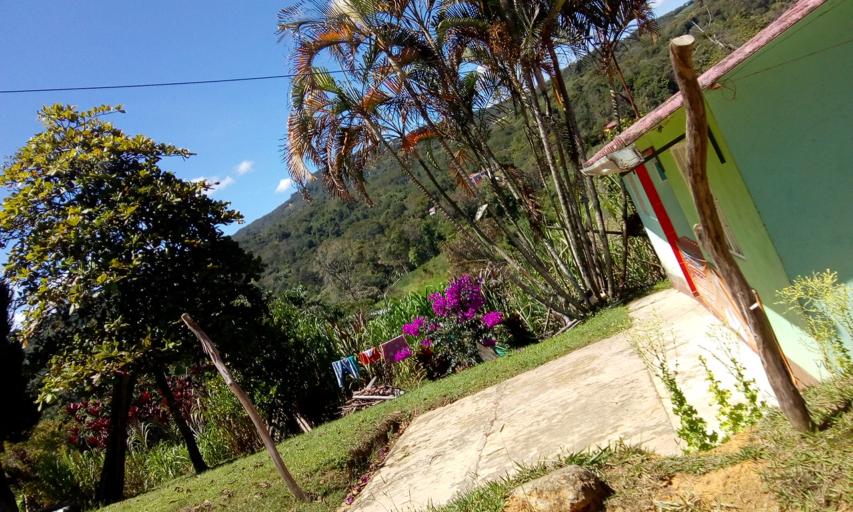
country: CO
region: Santander
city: Guepsa
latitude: 6.0076
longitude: -73.5482
